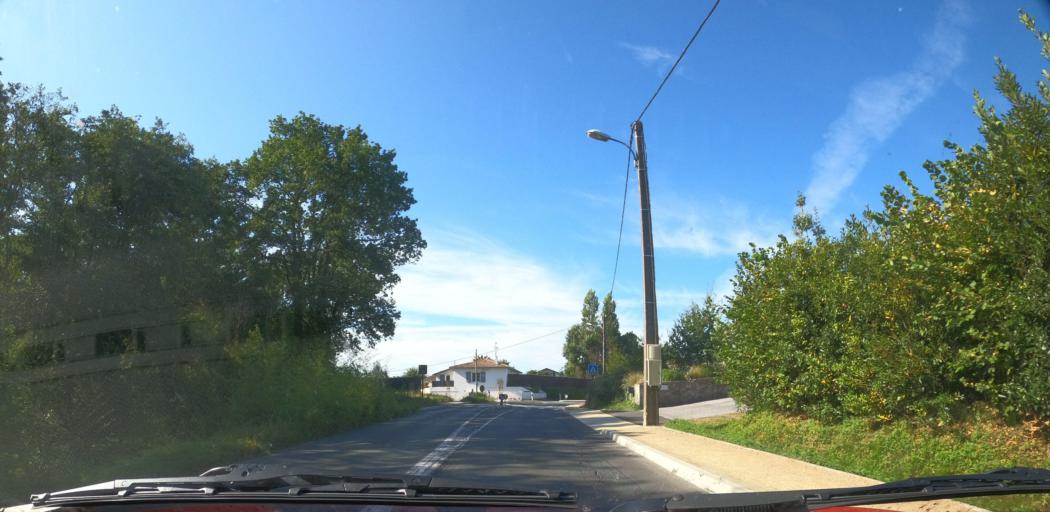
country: FR
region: Aquitaine
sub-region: Departement des Pyrenees-Atlantiques
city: Arbonne
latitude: 43.4400
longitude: -1.5471
